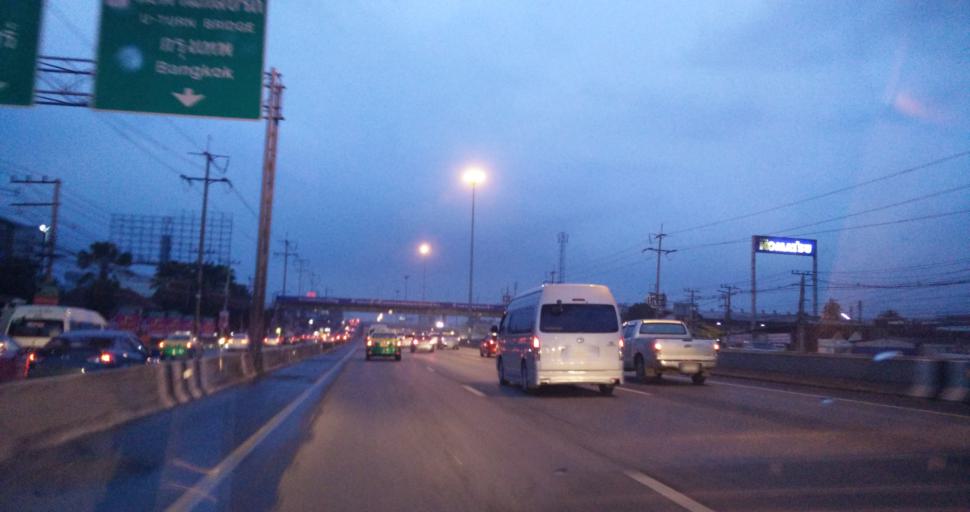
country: TH
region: Pathum Thani
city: Khlong Luang
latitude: 14.0291
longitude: 100.6158
